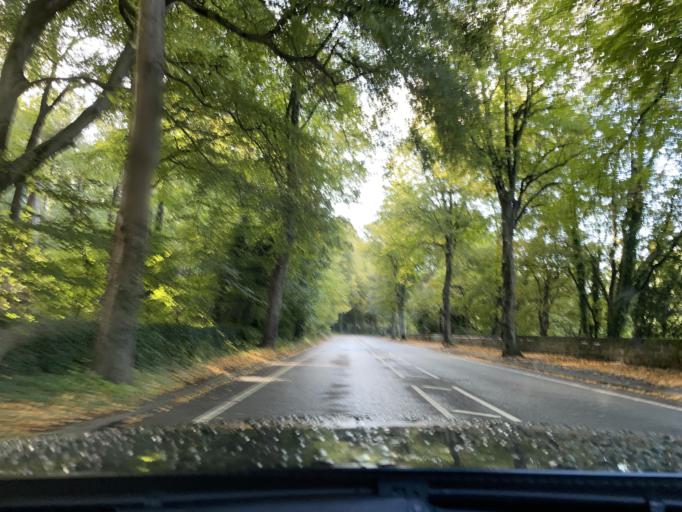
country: GB
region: England
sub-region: Sheffield
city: Oughtibridge
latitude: 53.3963
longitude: -1.5122
